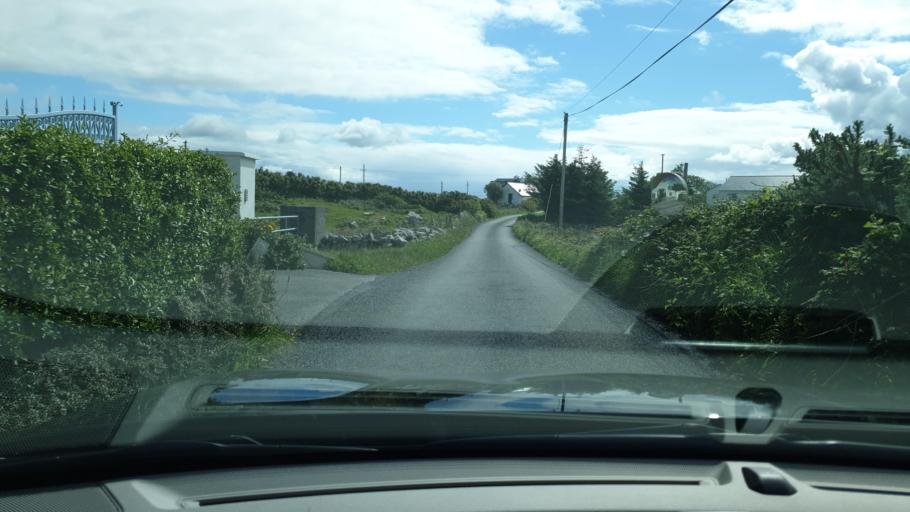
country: IE
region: Connaught
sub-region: County Galway
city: Clifden
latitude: 53.4363
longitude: -10.0752
